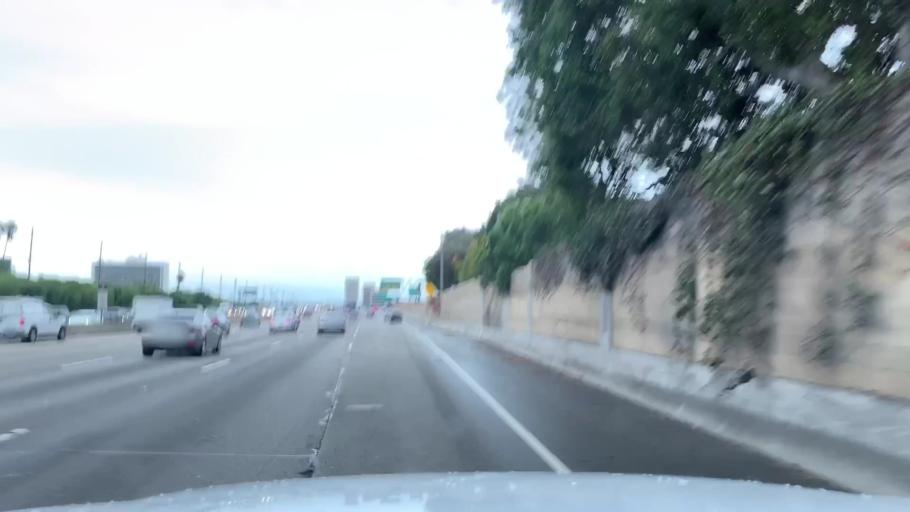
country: US
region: California
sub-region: Los Angeles County
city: Westwood, Los Angeles
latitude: 34.0632
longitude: -118.4585
